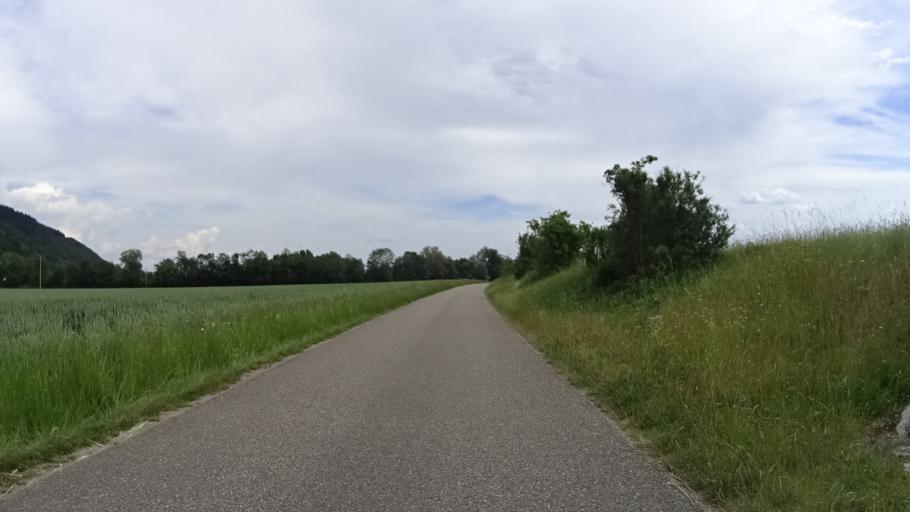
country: DE
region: Bavaria
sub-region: Upper Palatinate
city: Donaustauf
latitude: 49.0211
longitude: 12.2582
